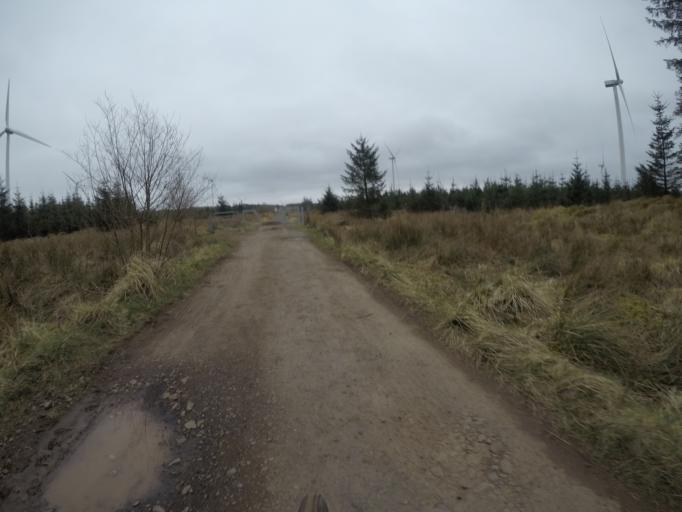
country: GB
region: Scotland
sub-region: East Ayrshire
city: Newmilns
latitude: 55.6581
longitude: -4.3320
